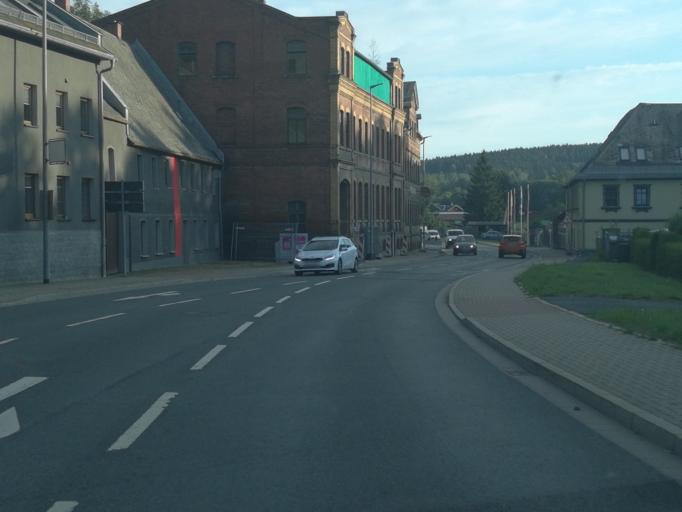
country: DE
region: Saxony
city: Adorf
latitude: 50.3222
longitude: 12.2574
